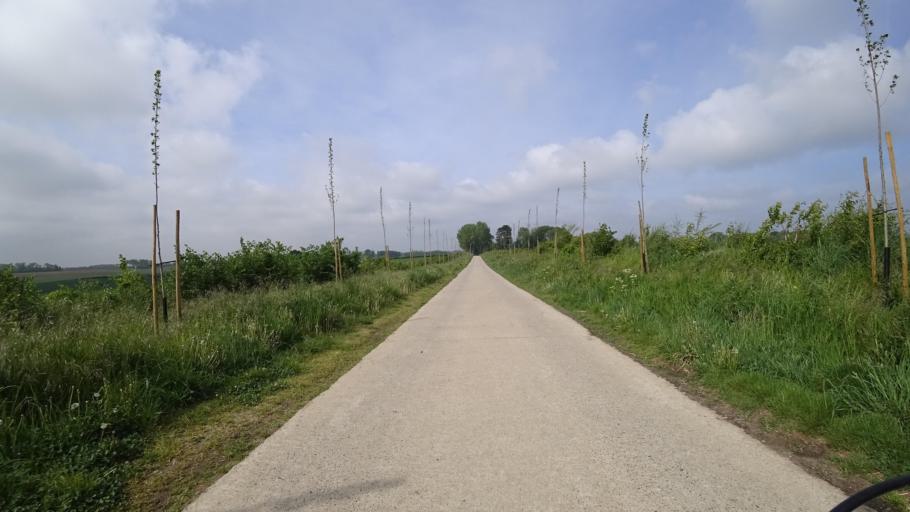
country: BE
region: Wallonia
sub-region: Province du Brabant Wallon
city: Louvain-la-Neuve
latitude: 50.6772
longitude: 4.6661
